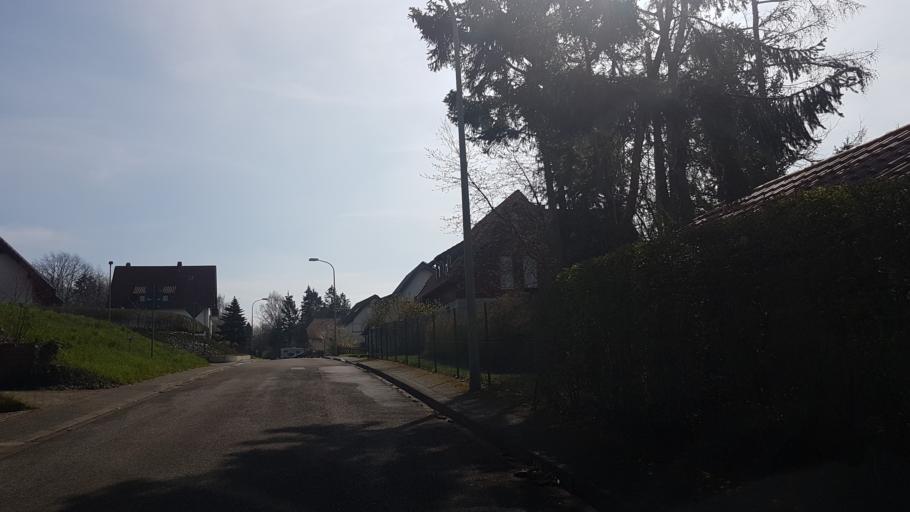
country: DE
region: Rheinland-Pfalz
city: Breitenbach
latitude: 49.4338
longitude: 7.2769
